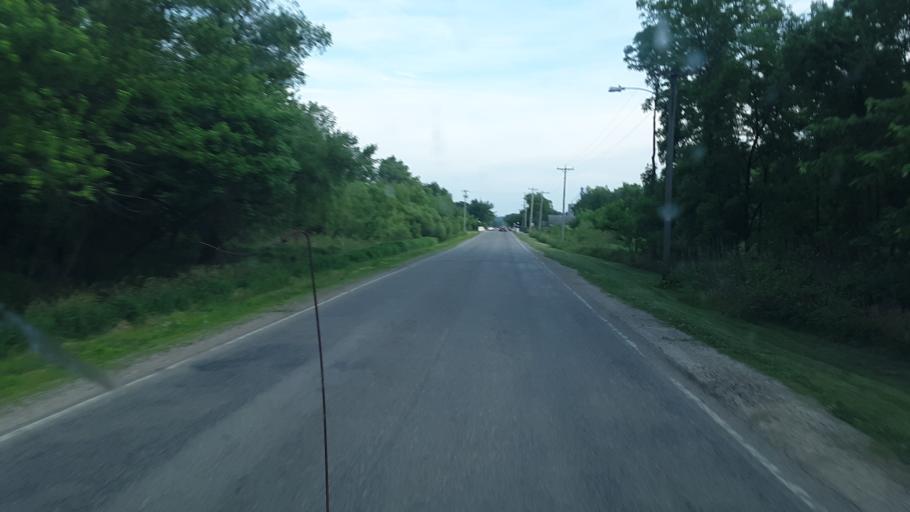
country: US
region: Iowa
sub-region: Benton County
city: Belle Plaine
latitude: 41.9236
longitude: -92.3946
